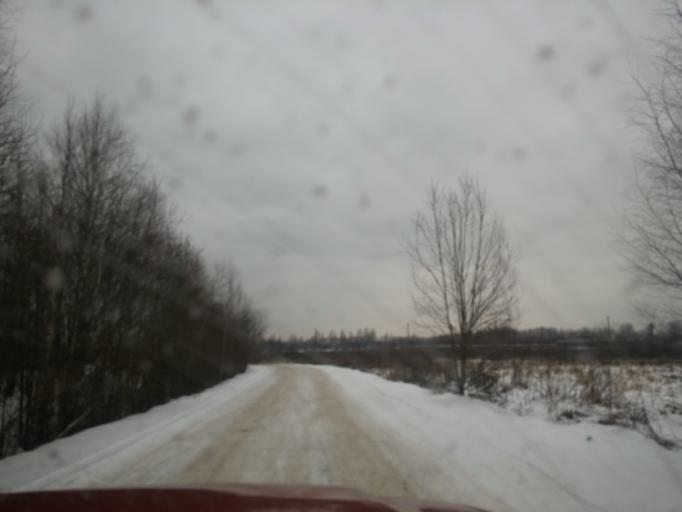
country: RU
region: Moskovskaya
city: Reshetnikovo
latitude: 56.4564
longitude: 36.5496
